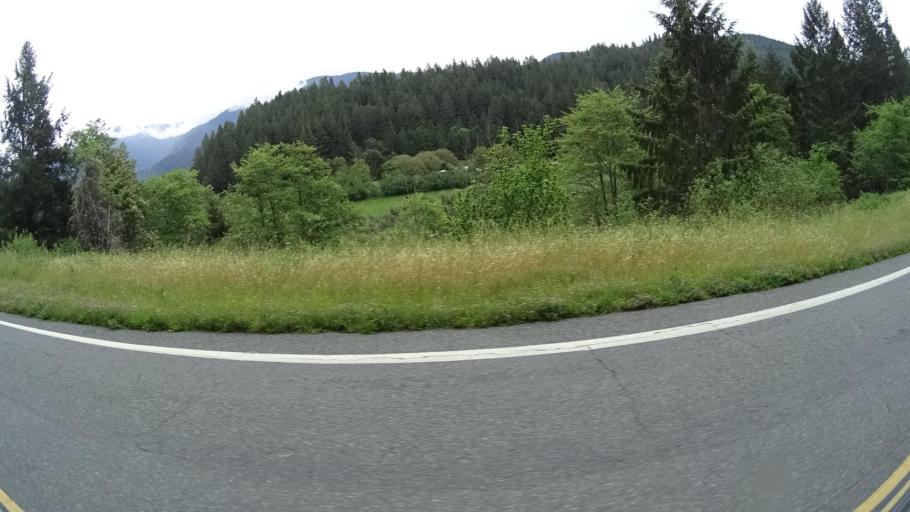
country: US
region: California
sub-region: Humboldt County
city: Willow Creek
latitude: 41.2934
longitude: -123.5708
